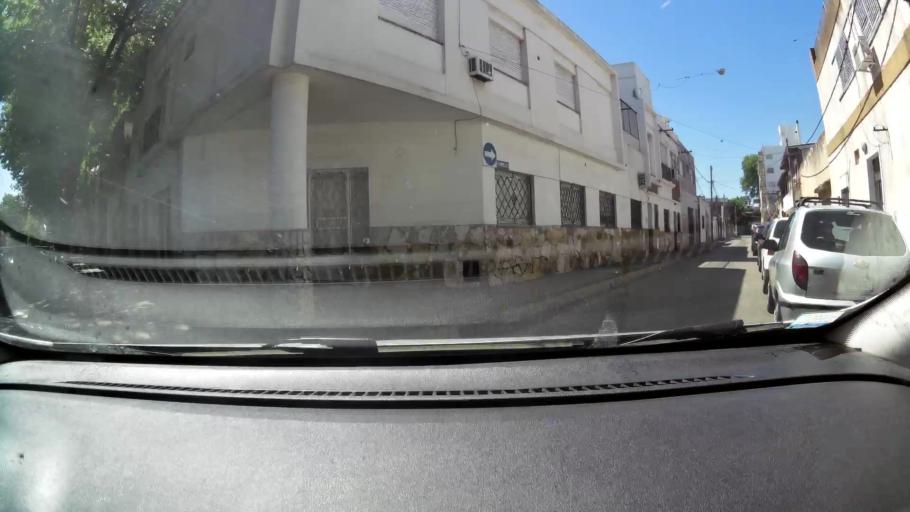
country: AR
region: Santa Fe
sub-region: Departamento de Rosario
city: Rosario
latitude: -32.9427
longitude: -60.6808
